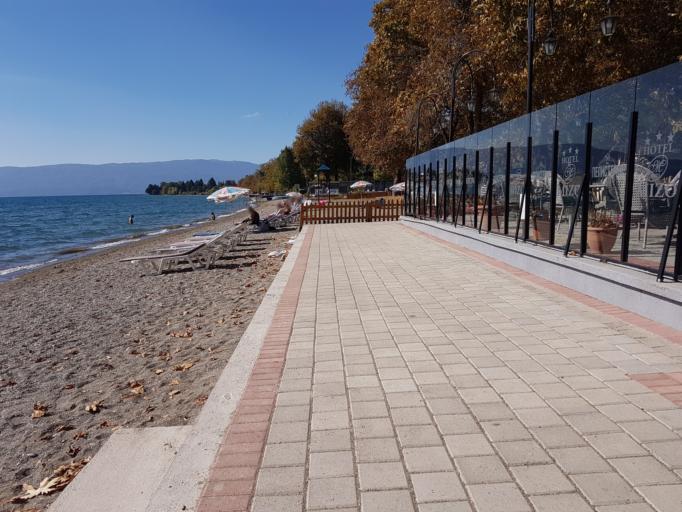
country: MK
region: Ohrid
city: Ohrid
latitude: 41.1190
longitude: 20.7842
